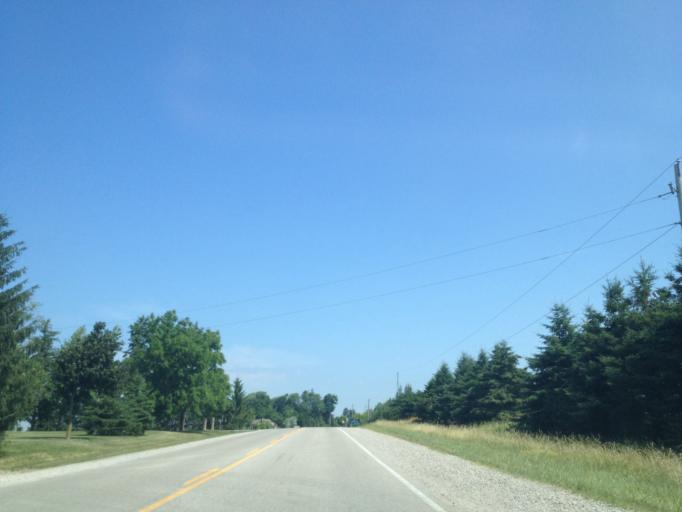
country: CA
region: Ontario
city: London
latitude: 43.2085
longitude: -81.2434
